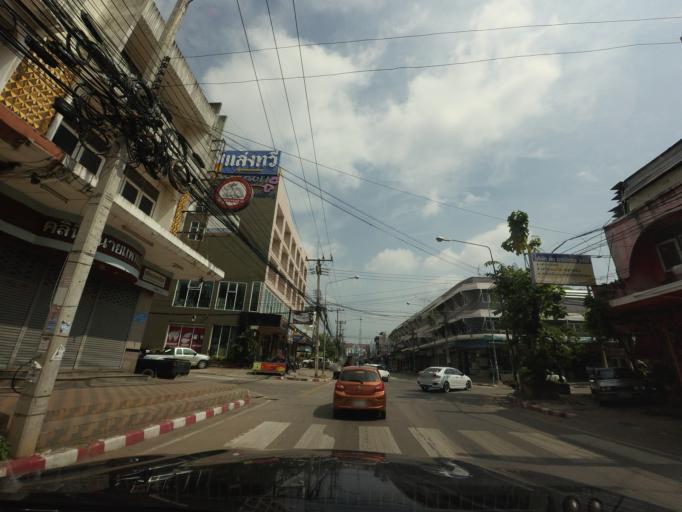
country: TH
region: Khon Kaen
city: Khon Kaen
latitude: 16.4369
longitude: 102.8302
